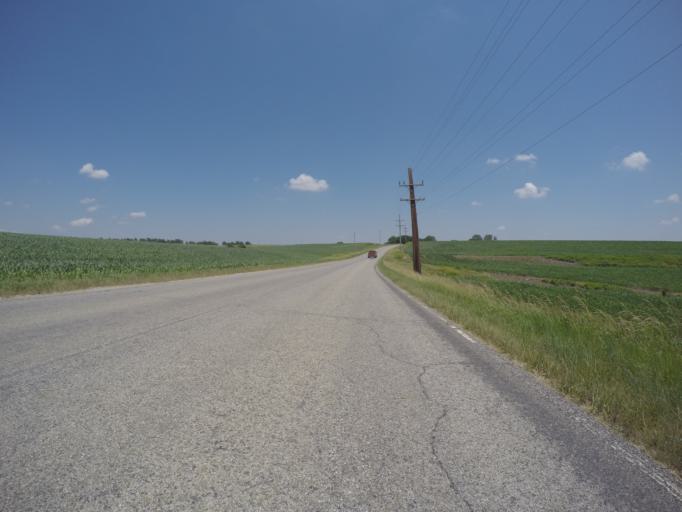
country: US
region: Kansas
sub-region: Doniphan County
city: Troy
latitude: 39.7663
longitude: -95.1289
